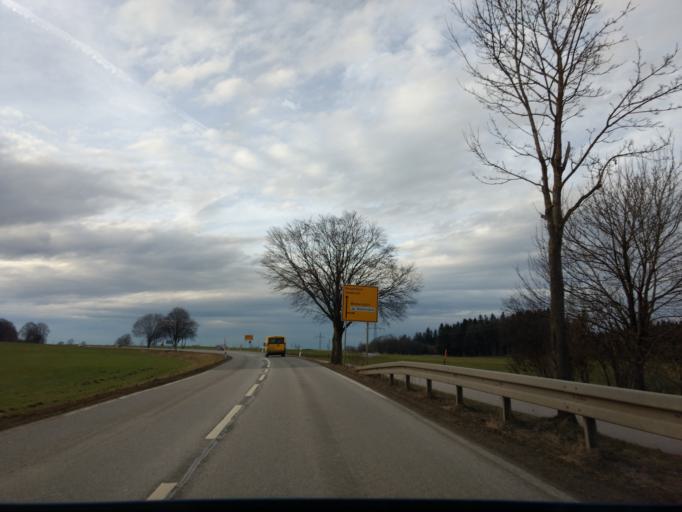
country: DE
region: Bavaria
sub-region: Upper Bavaria
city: Vachendorf
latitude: 47.8704
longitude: 12.6133
